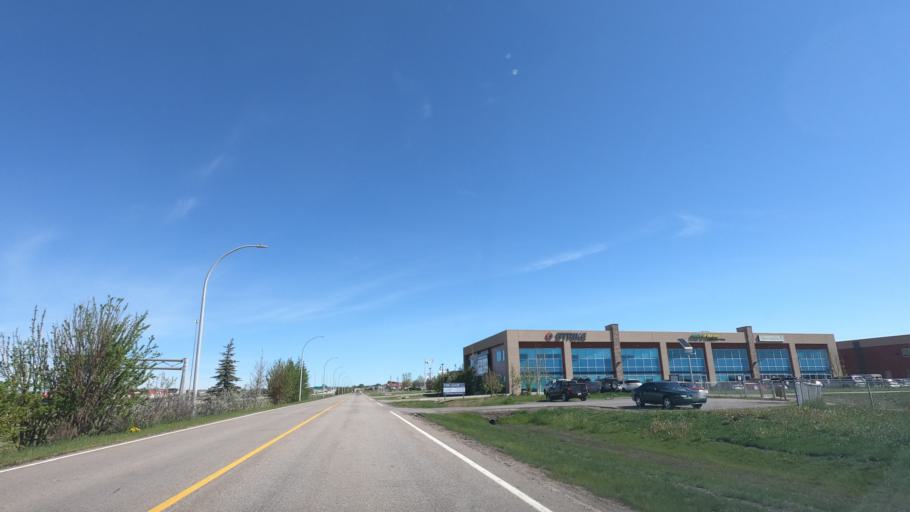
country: CA
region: Alberta
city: Airdrie
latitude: 51.2586
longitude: -114.0005
